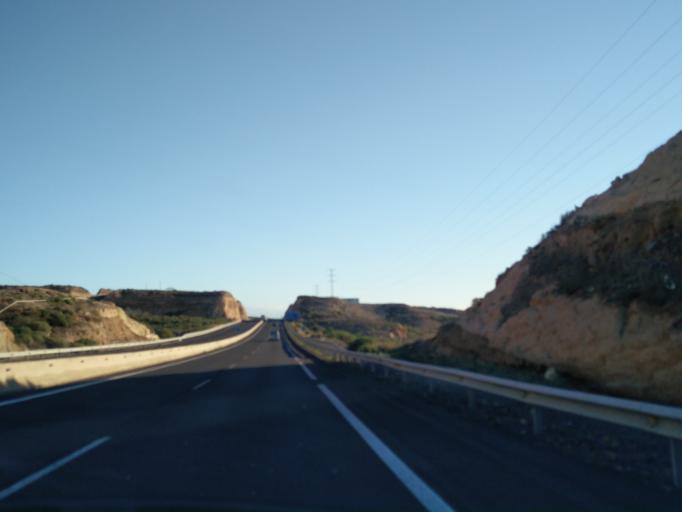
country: ES
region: Canary Islands
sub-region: Provincia de Santa Cruz de Tenerife
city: Lomo de Arico
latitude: 28.1123
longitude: -16.4830
